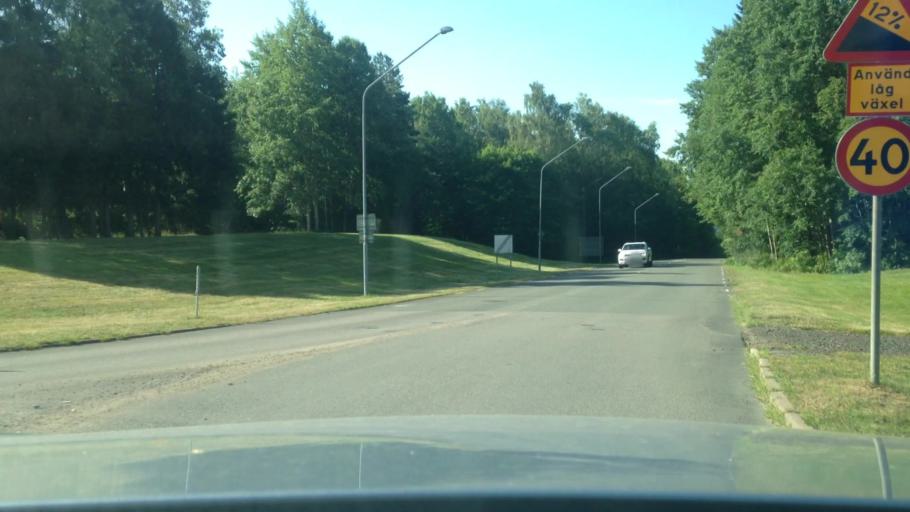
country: SE
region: Vaestra Goetaland
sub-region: Skovde Kommun
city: Skoevde
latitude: 58.4016
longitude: 13.8192
